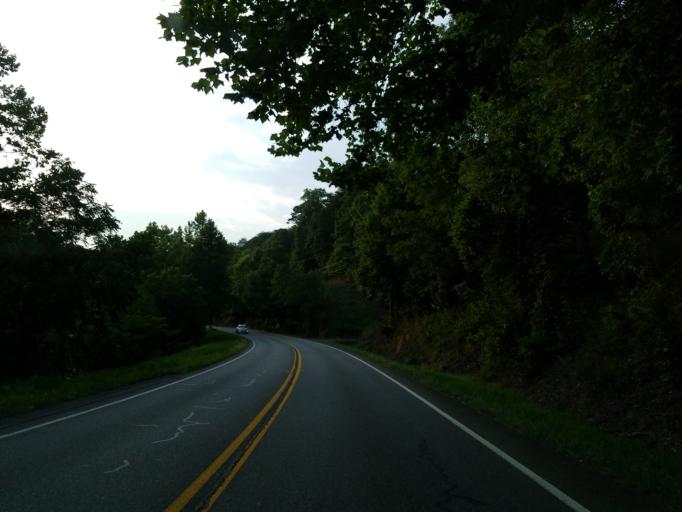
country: US
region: Georgia
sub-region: Gilmer County
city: Ellijay
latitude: 34.6835
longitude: -84.4579
